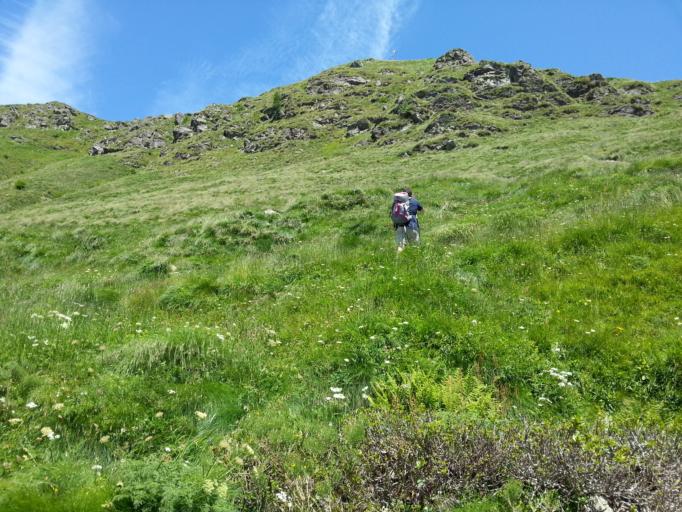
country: IT
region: Lombardy
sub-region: Provincia di Bergamo
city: Valtorta
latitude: 46.0235
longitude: 9.5000
